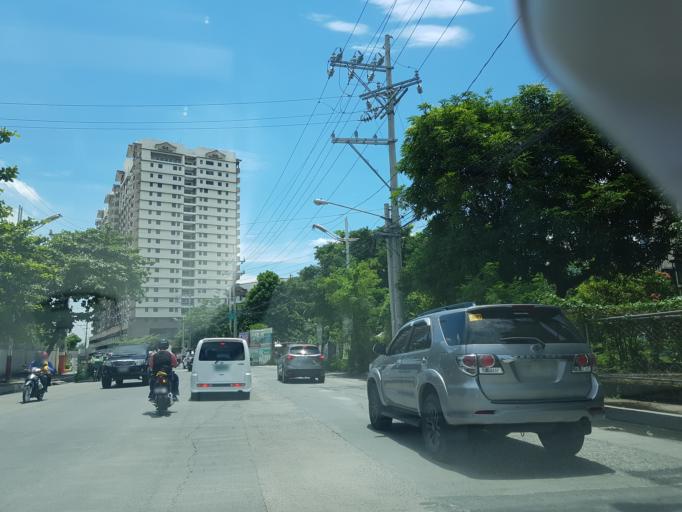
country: PH
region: Calabarzon
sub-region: Province of Rizal
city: Pateros
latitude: 14.5294
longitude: 121.0614
